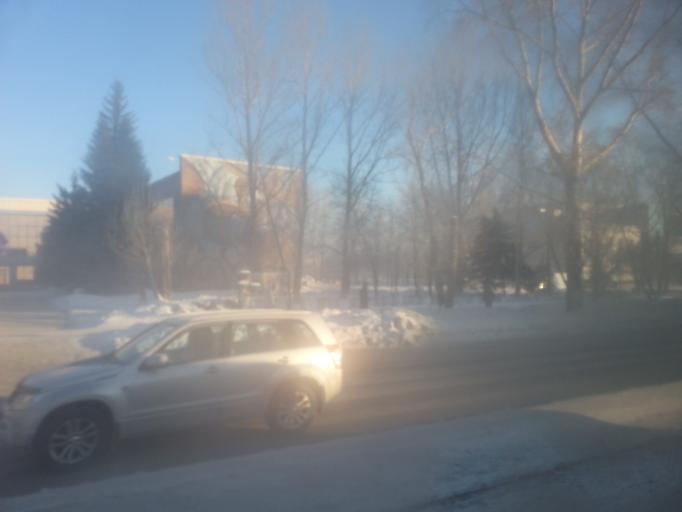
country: RU
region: Altai Krai
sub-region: Gorod Barnaulskiy
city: Barnaul
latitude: 53.3568
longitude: 83.7108
